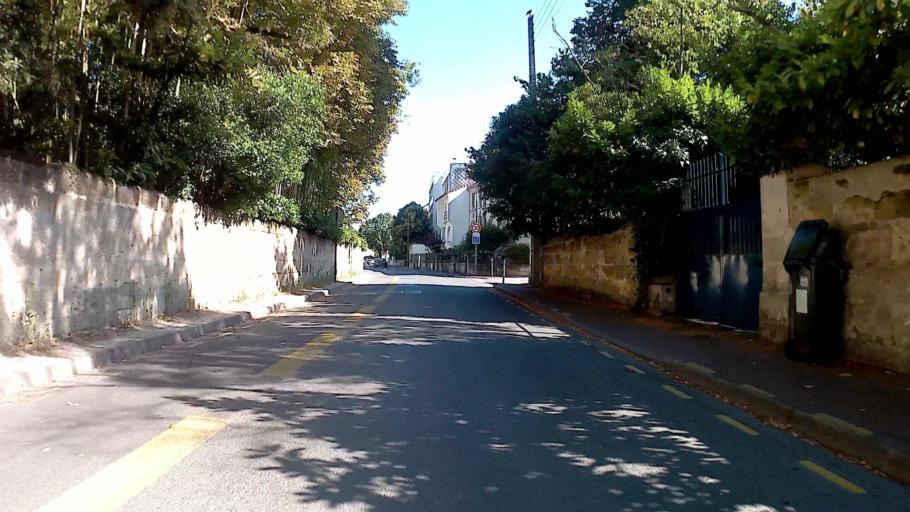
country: FR
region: Aquitaine
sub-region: Departement de la Gironde
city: Le Bouscat
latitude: 44.8585
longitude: -0.5966
